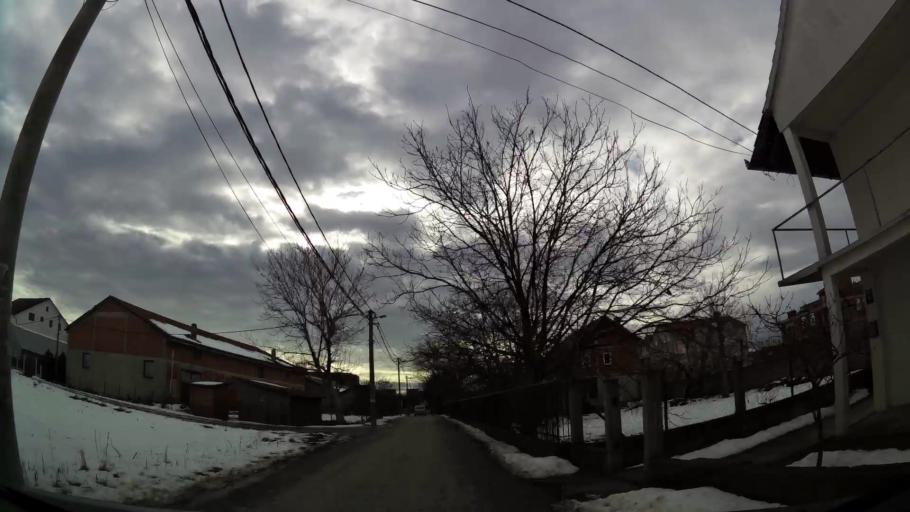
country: RS
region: Central Serbia
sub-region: Belgrade
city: Surcin
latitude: 44.8028
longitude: 20.3348
